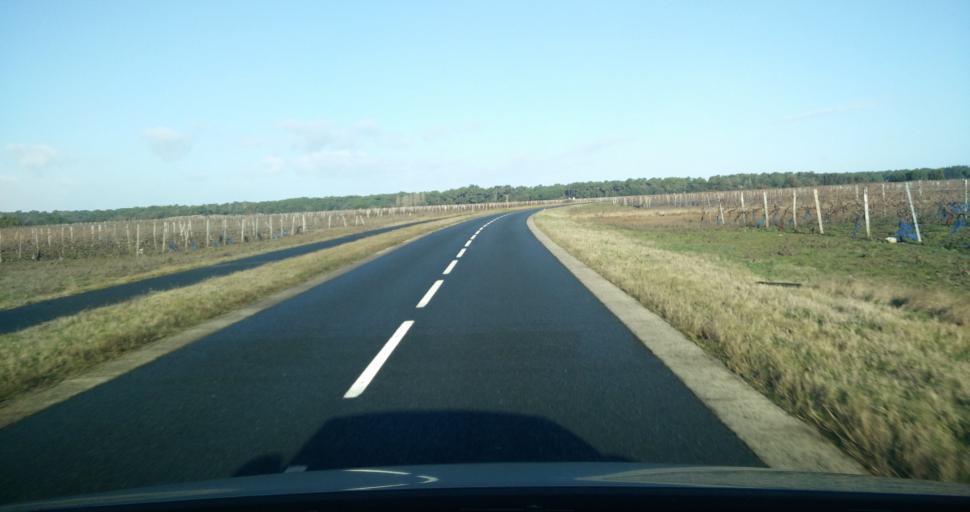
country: FR
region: Poitou-Charentes
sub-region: Departement de la Charente-Maritime
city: Sainte-Marie-de-Re
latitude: 46.1618
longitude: -1.3209
